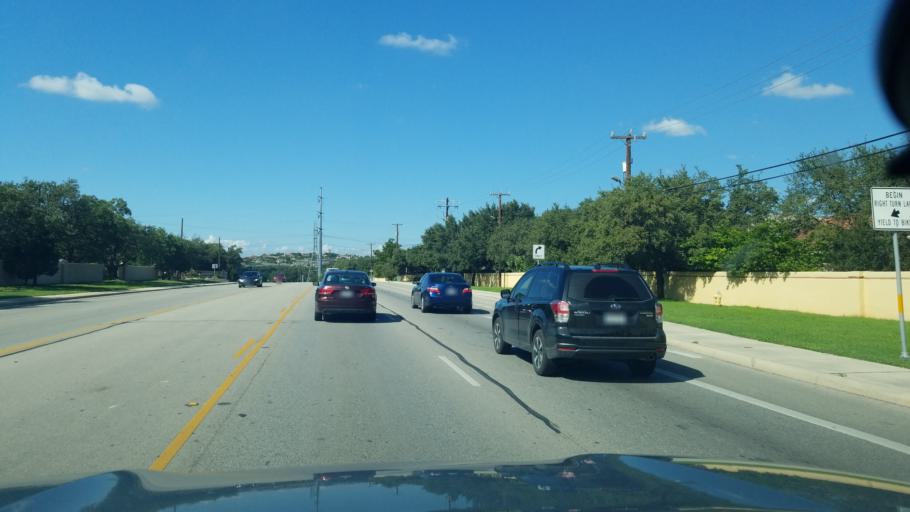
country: US
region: Texas
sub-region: Bexar County
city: Hollywood Park
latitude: 29.6151
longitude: -98.5096
